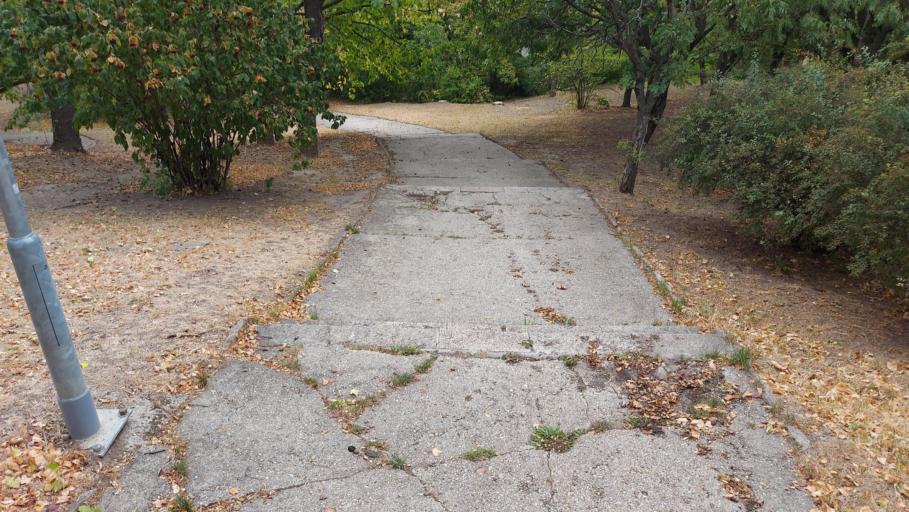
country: HU
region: Budapest
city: Budapest XI. keruelet
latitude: 47.4844
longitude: 19.0453
